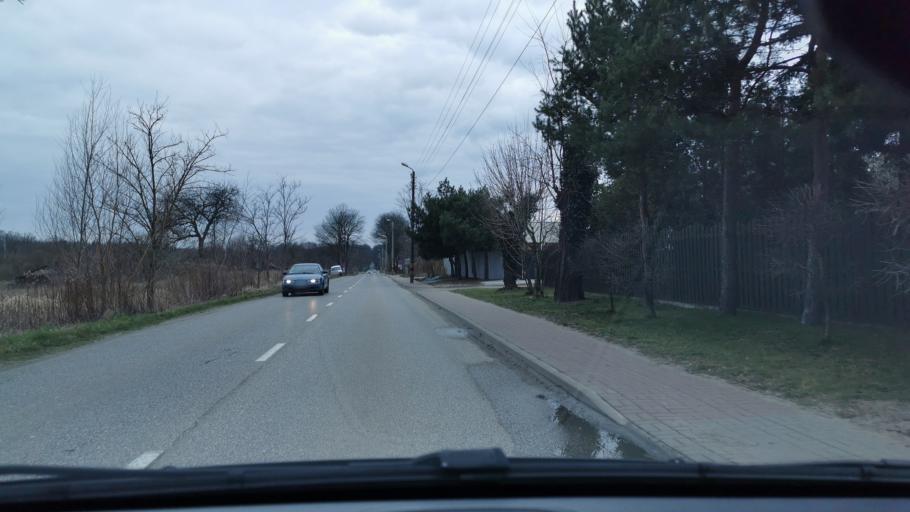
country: PL
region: Masovian Voivodeship
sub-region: Powiat zyrardowski
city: Radziejowice
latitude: 52.0108
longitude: 20.5273
